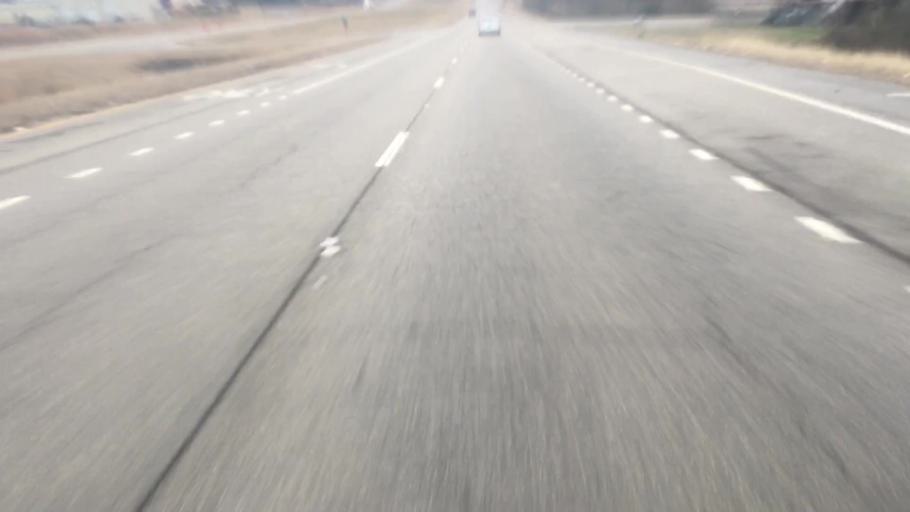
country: US
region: Alabama
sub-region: Walker County
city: Cordova
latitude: 33.8054
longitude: -87.1352
